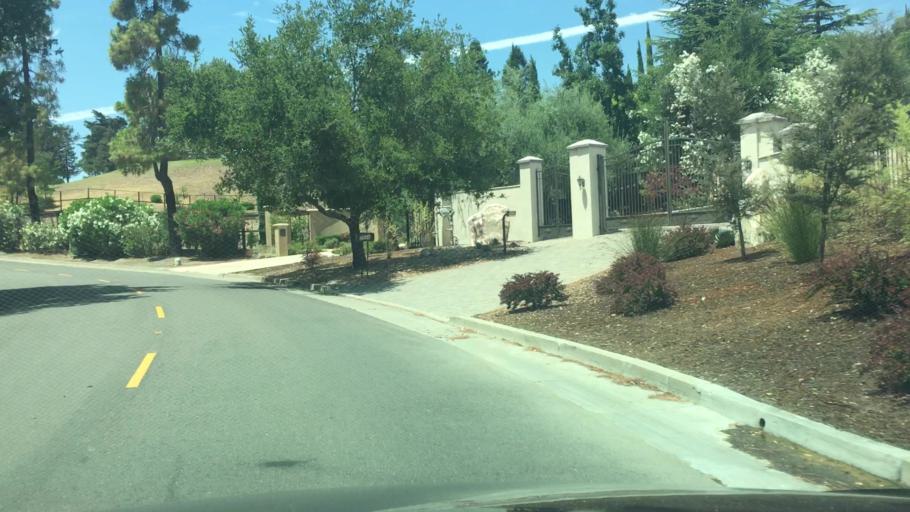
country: US
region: California
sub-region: Santa Clara County
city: Los Altos Hills
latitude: 37.3775
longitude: -122.1695
